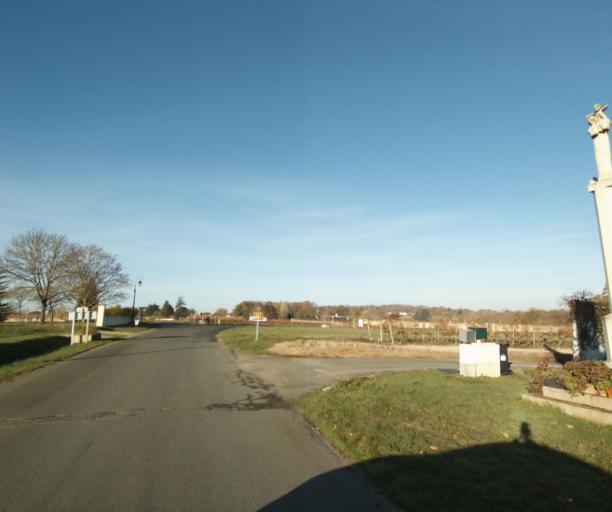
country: FR
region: Poitou-Charentes
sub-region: Departement de la Charente-Maritime
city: Cherac
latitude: 45.7054
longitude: -0.4426
